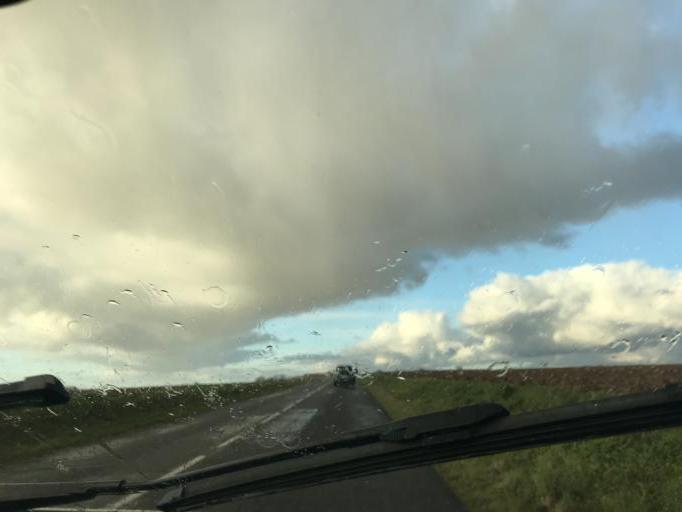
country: FR
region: Ile-de-France
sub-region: Departement de Seine-et-Marne
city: Claye-Souilly
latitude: 48.9757
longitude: 2.6977
